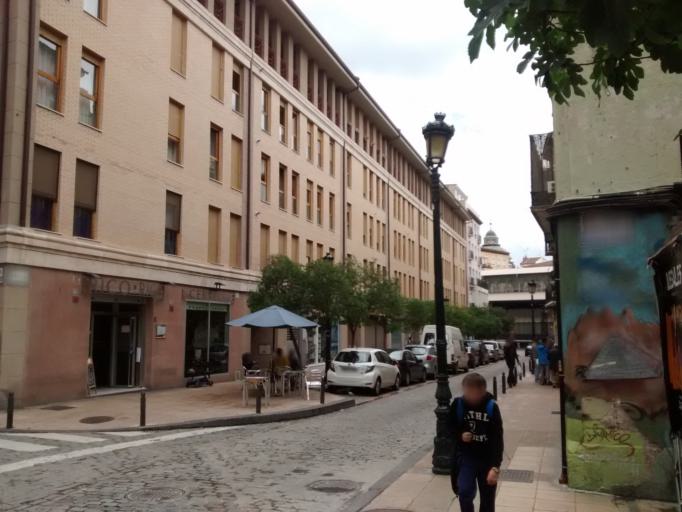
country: ES
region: Aragon
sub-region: Provincia de Zaragoza
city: Zaragoza
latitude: 41.6562
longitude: -0.8845
